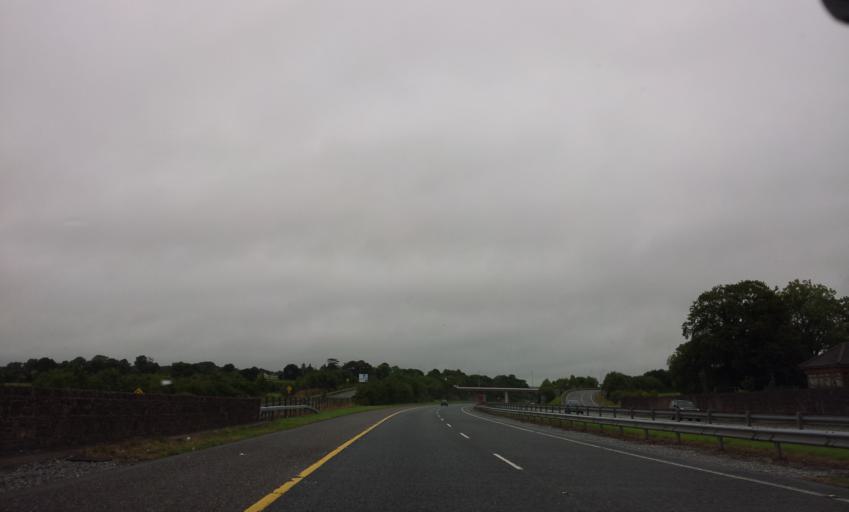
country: IE
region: Munster
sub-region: County Cork
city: Watergrasshill
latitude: 51.9516
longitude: -8.3907
